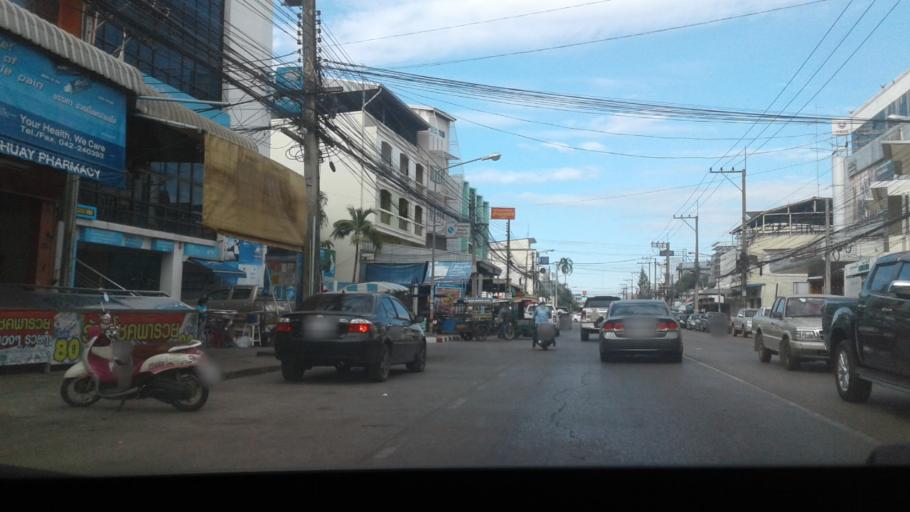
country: TH
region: Changwat Udon Thani
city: Udon Thani
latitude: 17.4184
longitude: 102.7912
